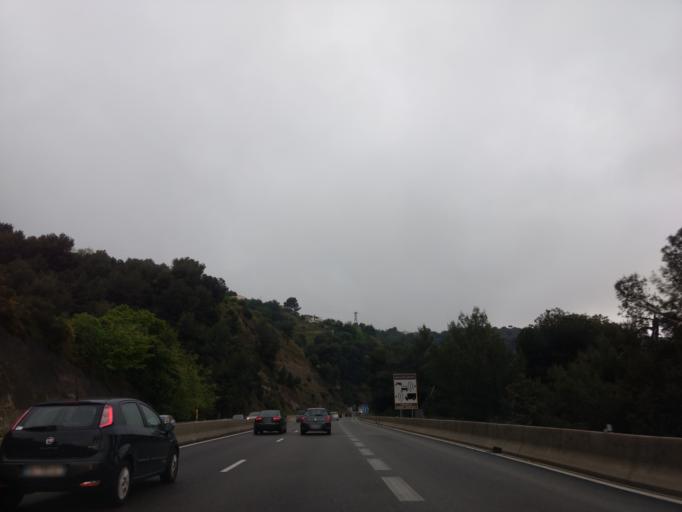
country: FR
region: Provence-Alpes-Cote d'Azur
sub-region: Departement des Alpes-Maritimes
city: Colomars
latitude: 43.7151
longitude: 7.2134
